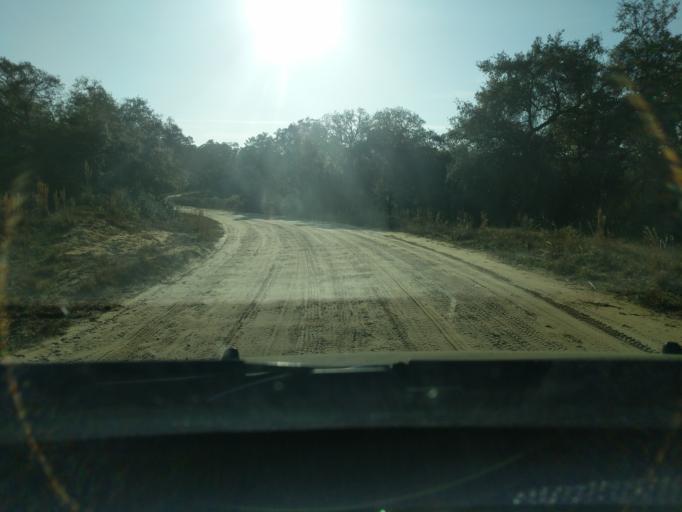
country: US
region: Florida
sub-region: Marion County
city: Silver Springs Shores
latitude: 29.2182
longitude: -81.8268
